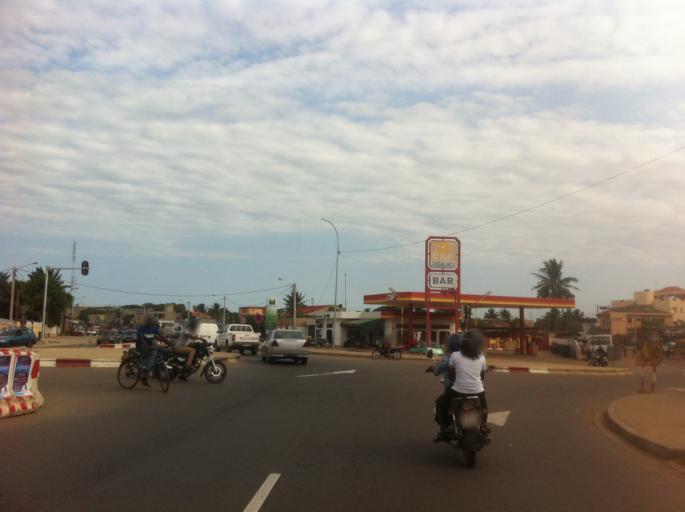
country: TG
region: Maritime
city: Lome
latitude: 6.1498
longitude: 1.2014
